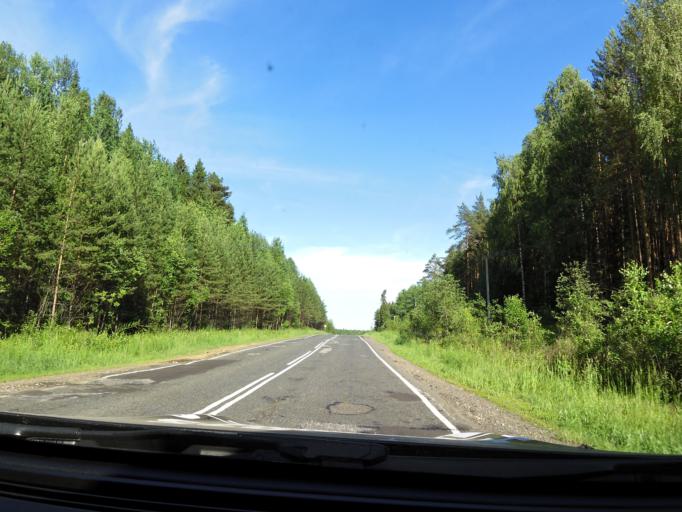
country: RU
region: Kirov
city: Belaya Kholunitsa
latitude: 58.9059
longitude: 51.0246
